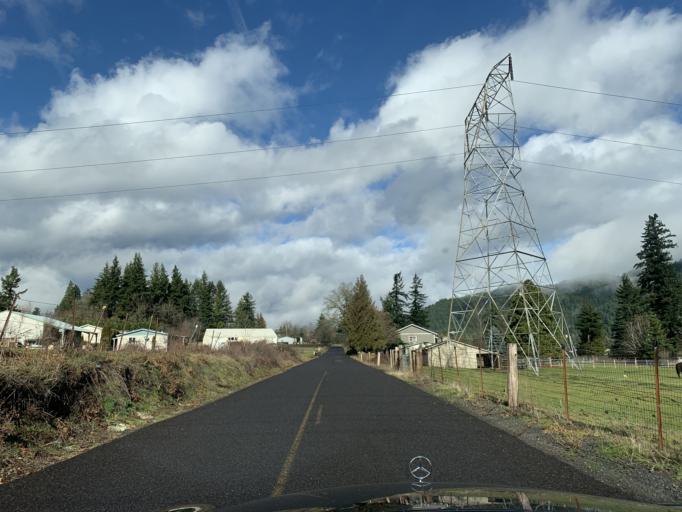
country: US
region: Washington
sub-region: Skamania County
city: Carson
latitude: 45.7225
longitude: -121.8073
